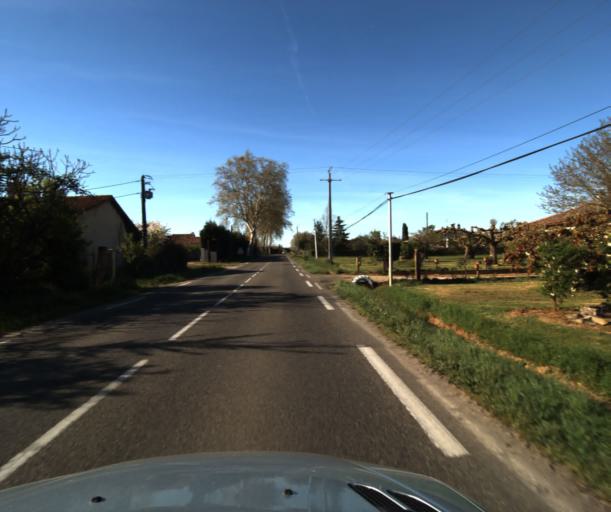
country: FR
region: Midi-Pyrenees
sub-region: Departement du Tarn-et-Garonne
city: Montbeton
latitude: 44.0631
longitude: 1.2881
